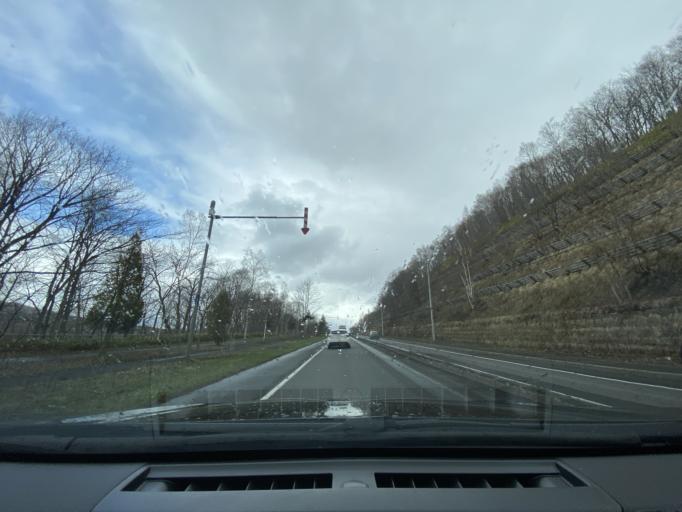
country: JP
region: Hokkaido
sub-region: Asahikawa-shi
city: Asahikawa
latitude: 43.7583
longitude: 142.2765
